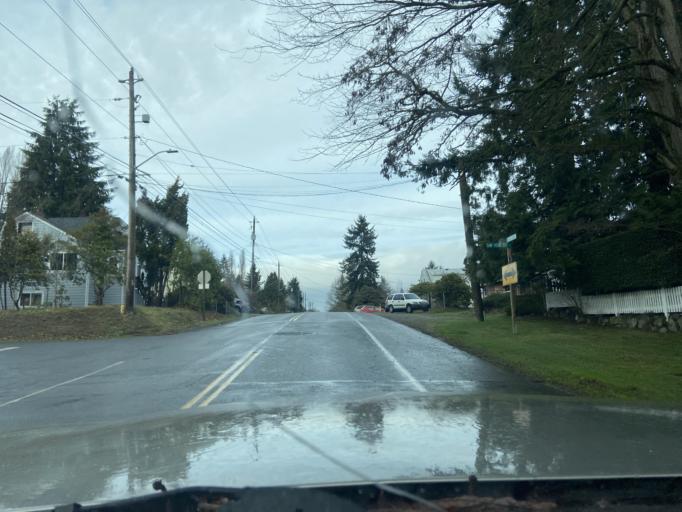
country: US
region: Washington
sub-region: King County
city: White Center
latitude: 47.5082
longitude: -122.3447
